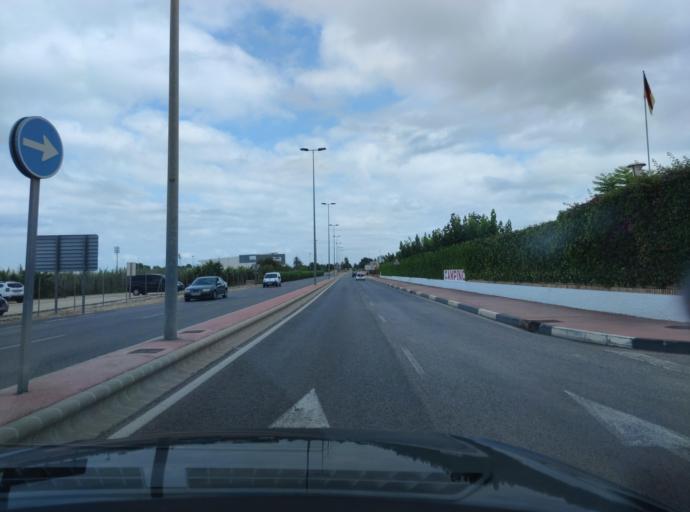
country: ES
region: Valencia
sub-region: Provincia de Alicante
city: Santa Pola
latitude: 38.2005
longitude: -0.5700
